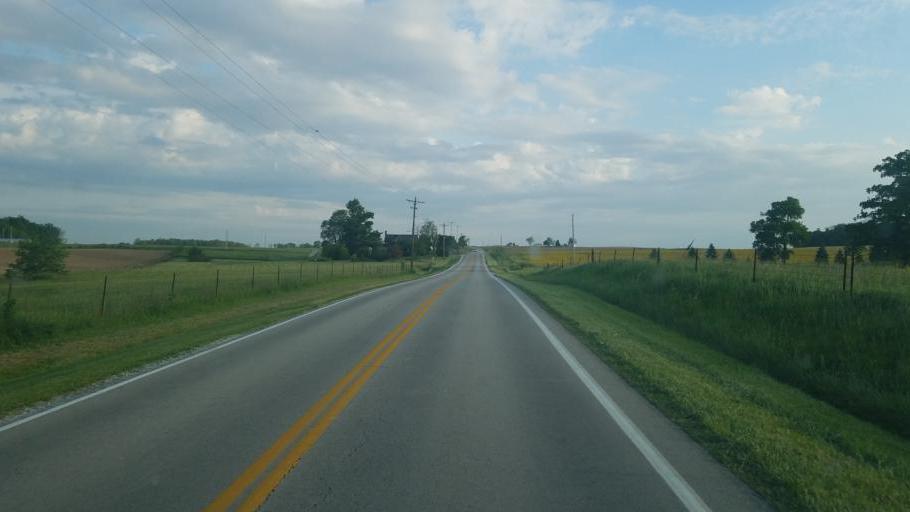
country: US
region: Ohio
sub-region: Highland County
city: Leesburg
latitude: 39.3953
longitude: -83.5975
